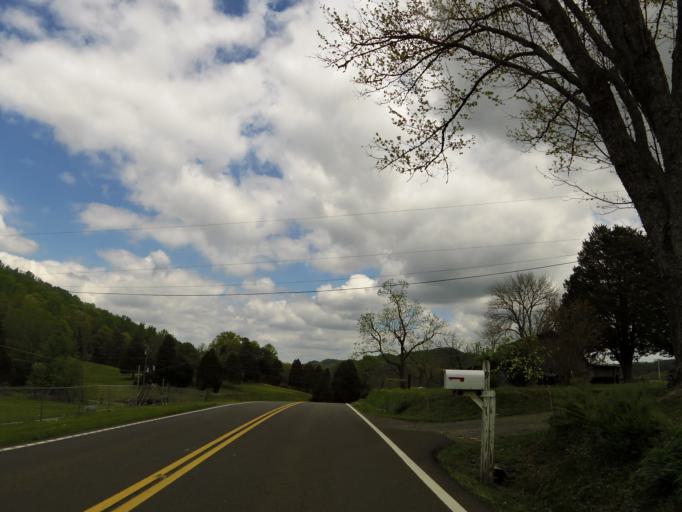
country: US
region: Tennessee
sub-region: Anderson County
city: Norris
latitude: 36.1227
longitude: -84.0083
